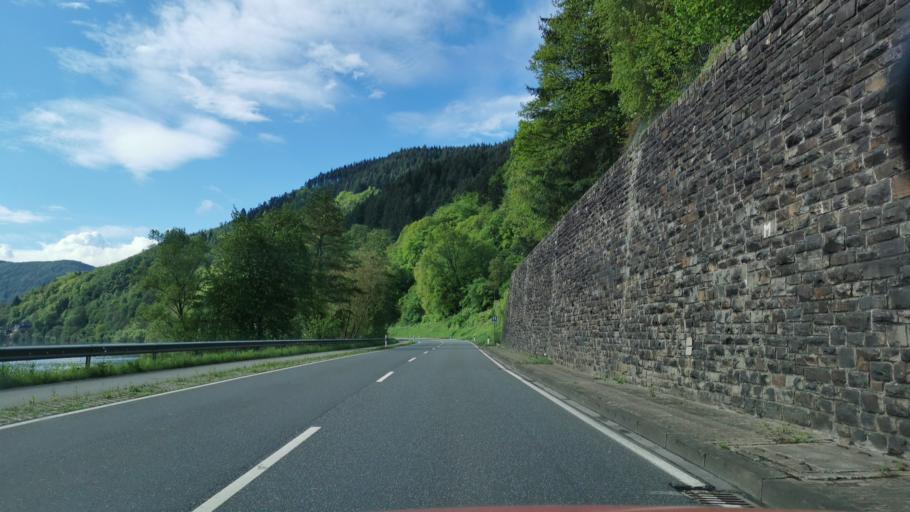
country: DE
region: Rheinland-Pfalz
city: Traben-Trarbach
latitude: 49.9604
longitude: 7.0995
